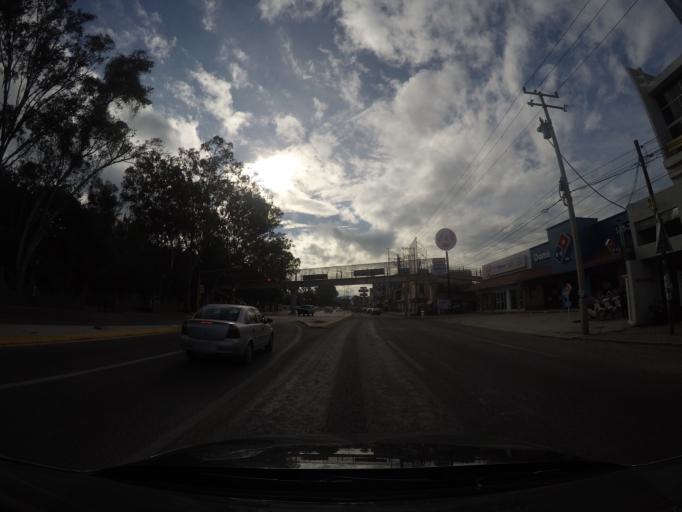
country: MX
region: Oaxaca
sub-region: Santa Cruz Amilpas
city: Santa Cruz Amilpas
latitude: 17.0689
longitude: -96.6975
